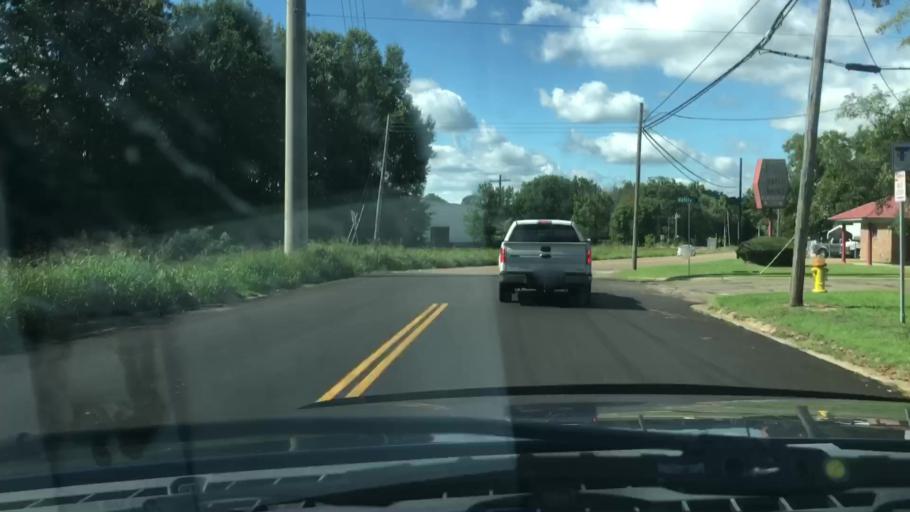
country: US
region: Texas
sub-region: Bowie County
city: Texarkana
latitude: 33.4194
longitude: -94.0588
